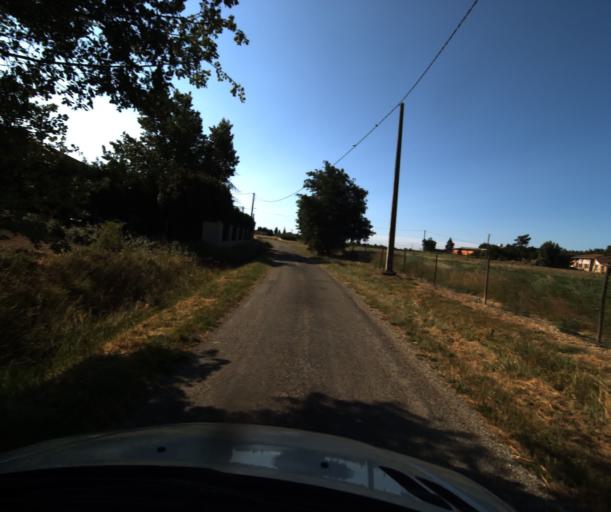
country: FR
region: Midi-Pyrenees
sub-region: Departement du Tarn-et-Garonne
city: Bressols
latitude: 43.9709
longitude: 1.2932
